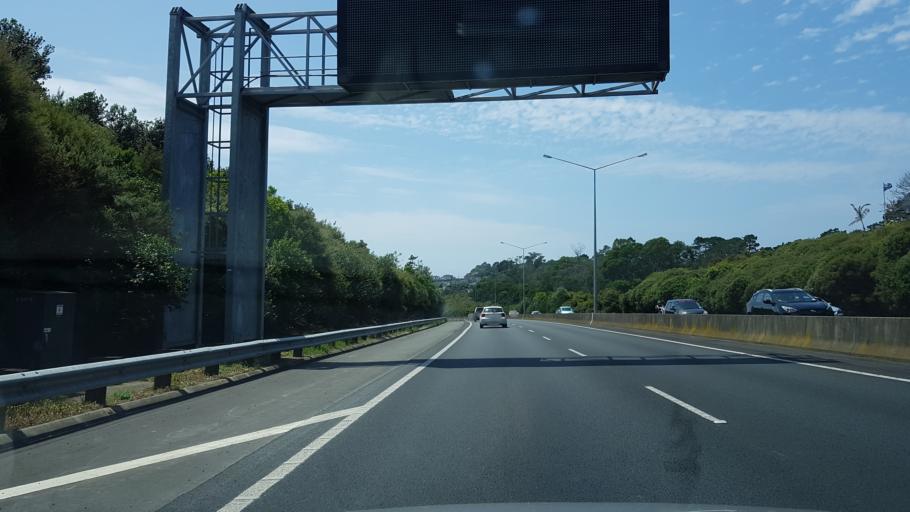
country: NZ
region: Auckland
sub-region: Auckland
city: North Shore
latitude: -36.7784
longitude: 174.6811
